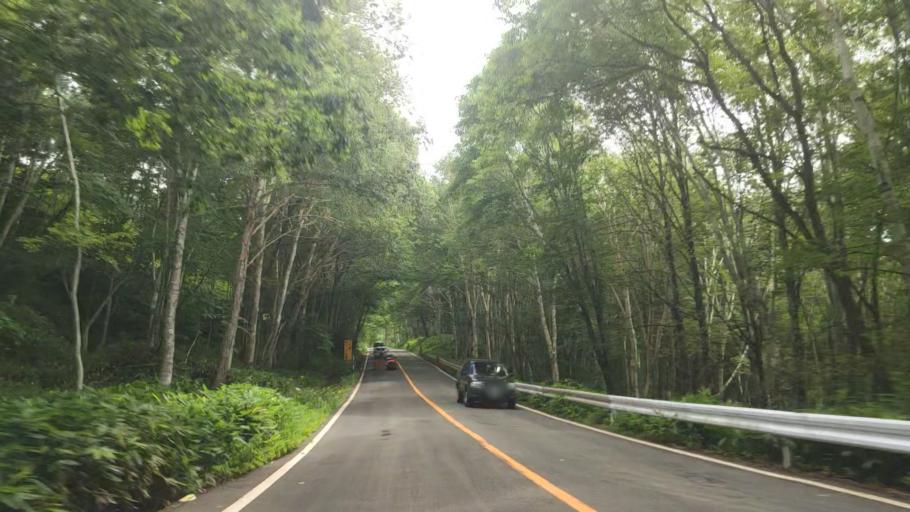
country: JP
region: Tochigi
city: Nikko
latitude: 36.8163
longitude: 139.3421
